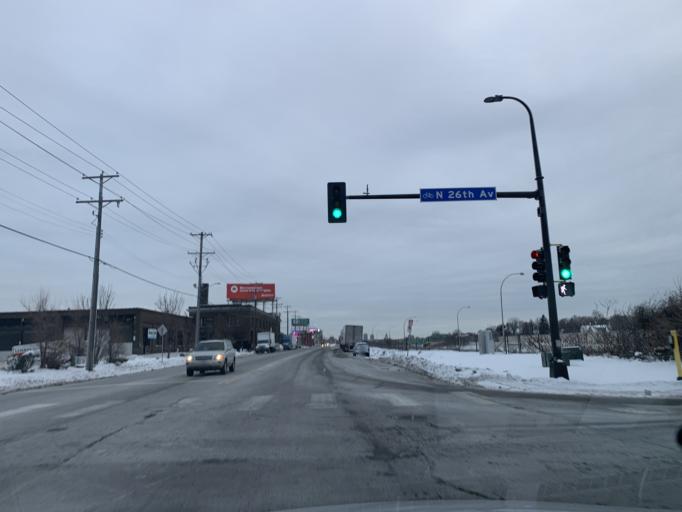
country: US
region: Minnesota
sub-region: Hennepin County
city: Minneapolis
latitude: 45.0060
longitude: -93.2819
